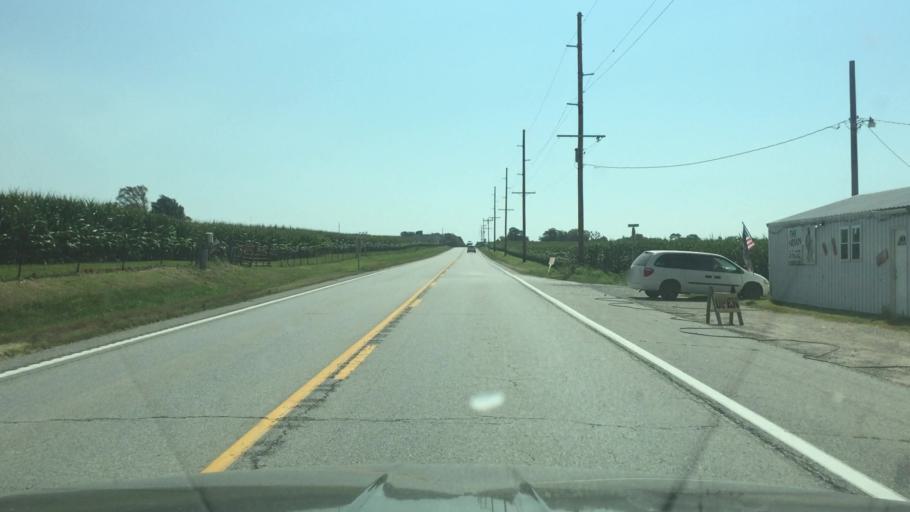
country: US
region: Missouri
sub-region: Moniteau County
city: Tipton
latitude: 38.6698
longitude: -92.8899
